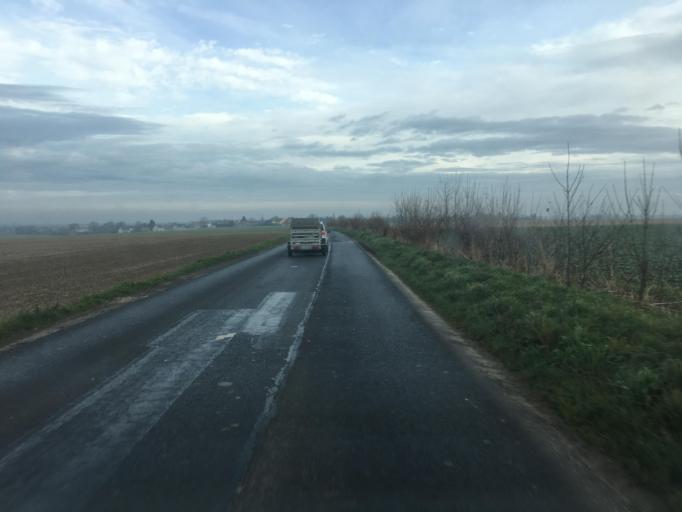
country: FR
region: Lower Normandy
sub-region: Departement du Calvados
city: Creully
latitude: 49.2418
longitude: -0.5722
